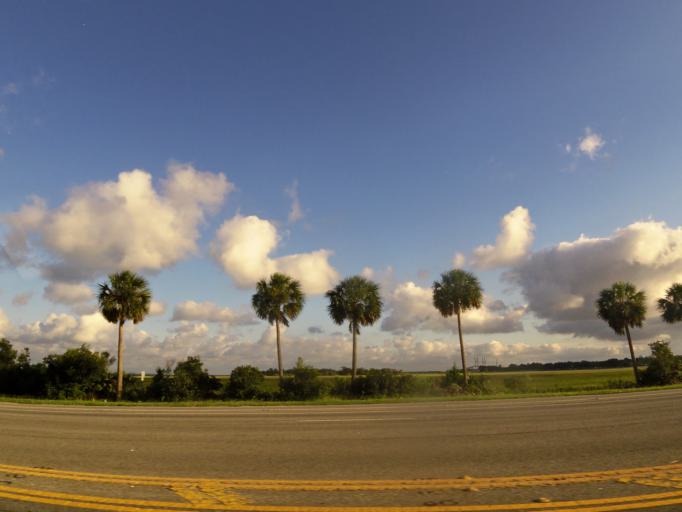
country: US
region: Georgia
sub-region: Glynn County
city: Brunswick
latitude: 31.1614
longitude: -81.4737
